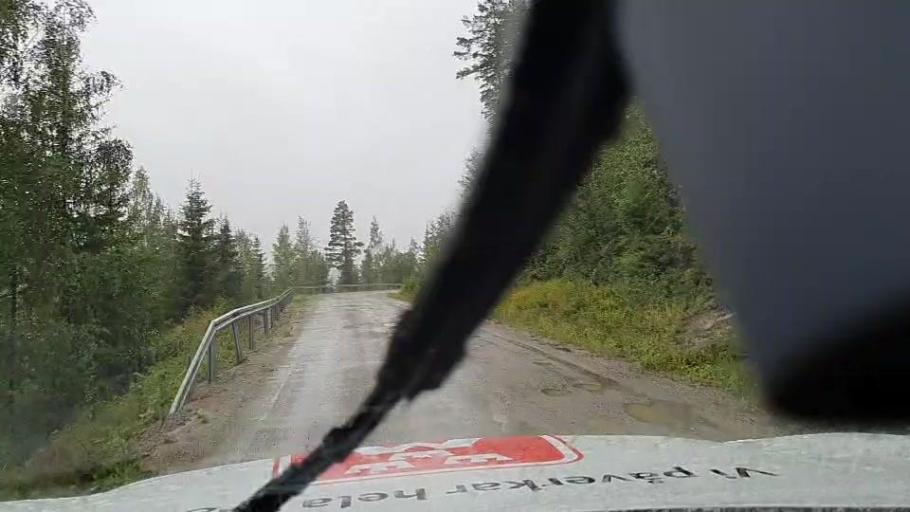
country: SE
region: Jaemtland
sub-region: OEstersunds Kommun
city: Brunflo
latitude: 62.8233
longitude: 15.0218
